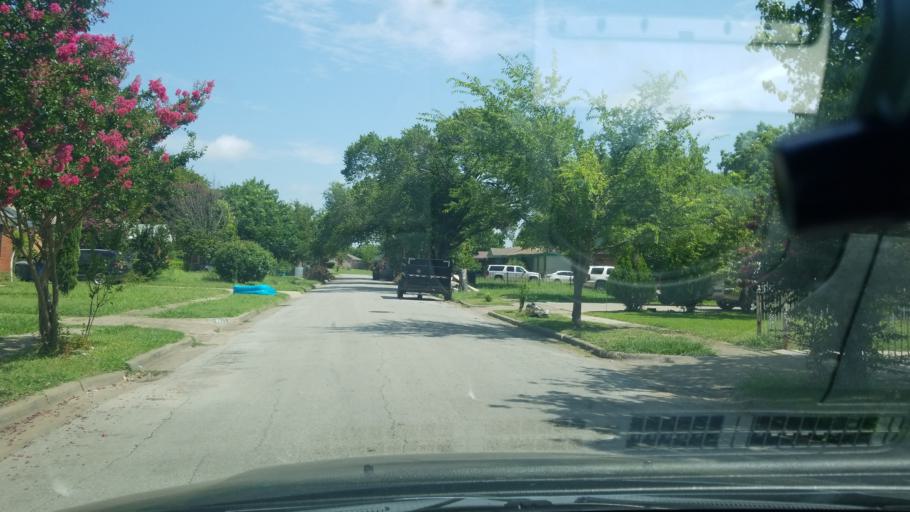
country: US
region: Texas
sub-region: Dallas County
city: Balch Springs
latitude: 32.7513
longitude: -96.6897
